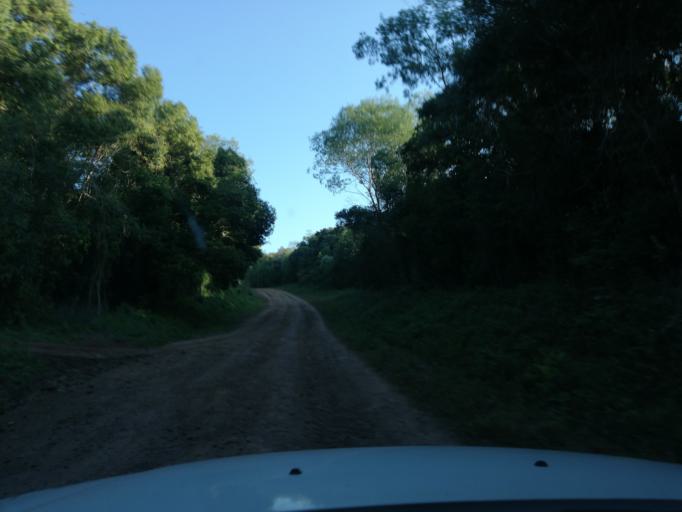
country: AR
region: Misiones
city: Cerro Cora
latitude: -27.6113
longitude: -55.7052
